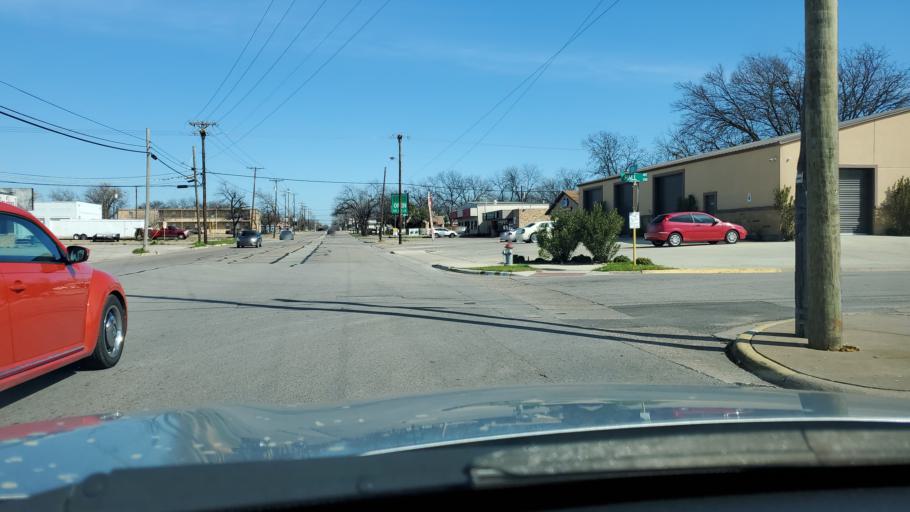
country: US
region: Texas
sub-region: Bell County
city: Killeen
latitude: 31.1203
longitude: -97.7253
